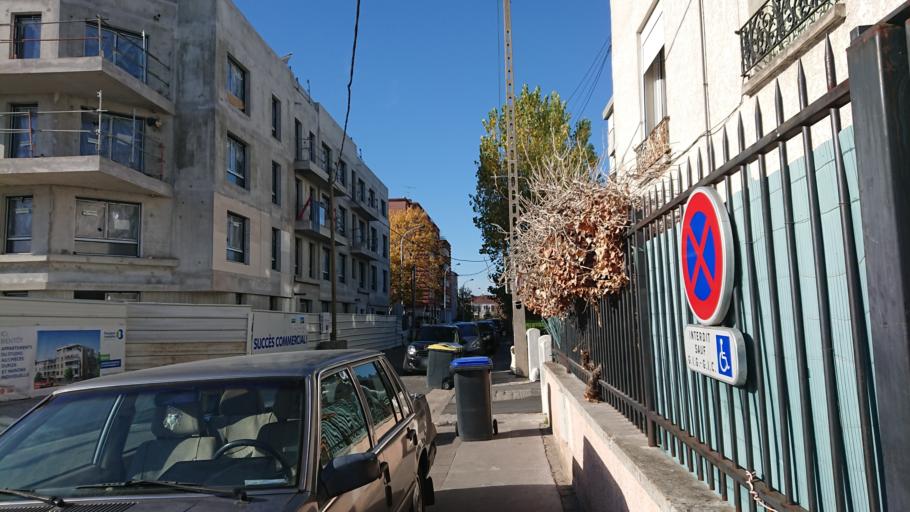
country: FR
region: Ile-de-France
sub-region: Departement des Hauts-de-Seine
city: Bois-Colombes
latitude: 48.9251
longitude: 2.2726
